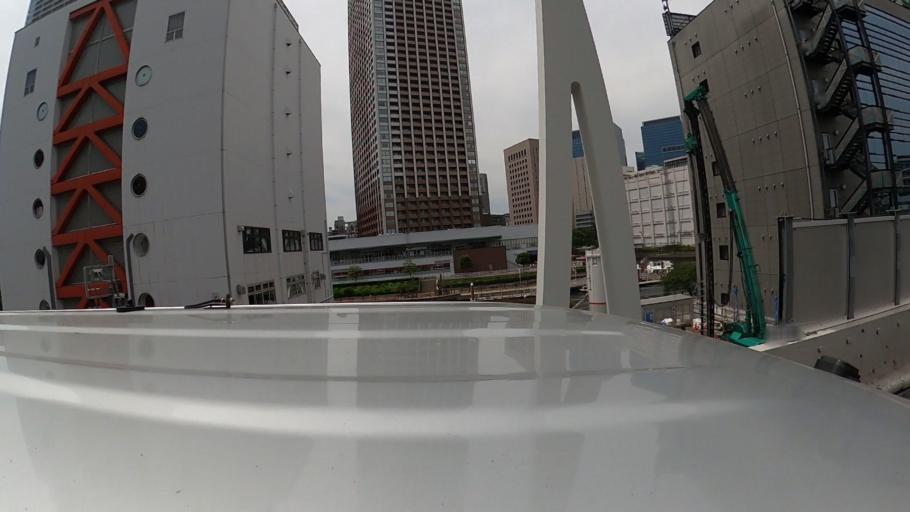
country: JP
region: Tokyo
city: Tokyo
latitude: 35.6410
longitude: 139.7539
